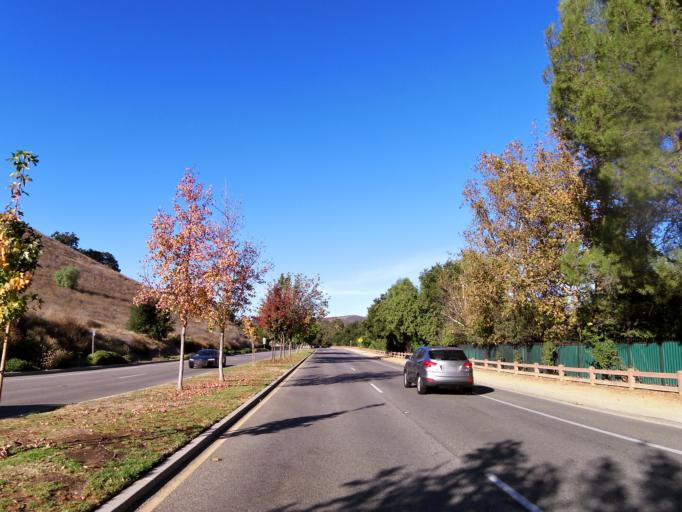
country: US
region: California
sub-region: Ventura County
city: Thousand Oaks
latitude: 34.1858
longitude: -118.8220
